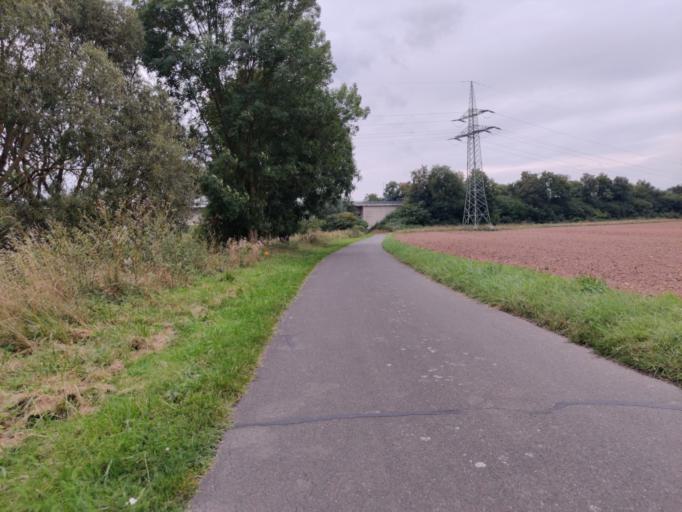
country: DE
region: Lower Saxony
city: Holzminden
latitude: 51.7996
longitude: 9.4203
